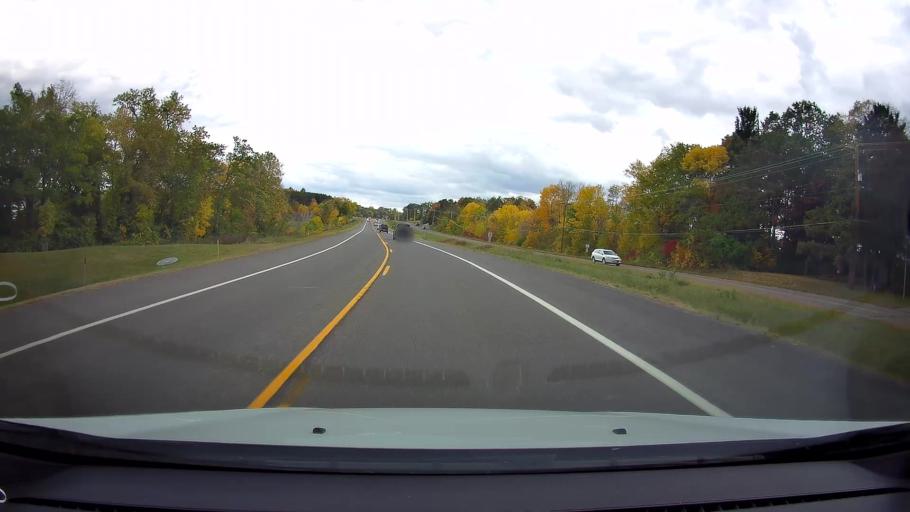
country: US
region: Minnesota
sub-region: Chisago County
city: Lindstrom
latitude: 45.3892
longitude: -92.8662
